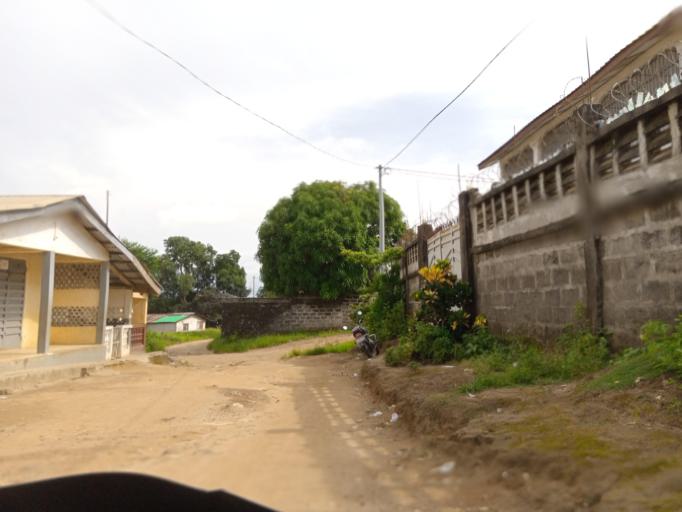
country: SL
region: Northern Province
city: Masoyila
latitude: 8.6076
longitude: -13.2029
